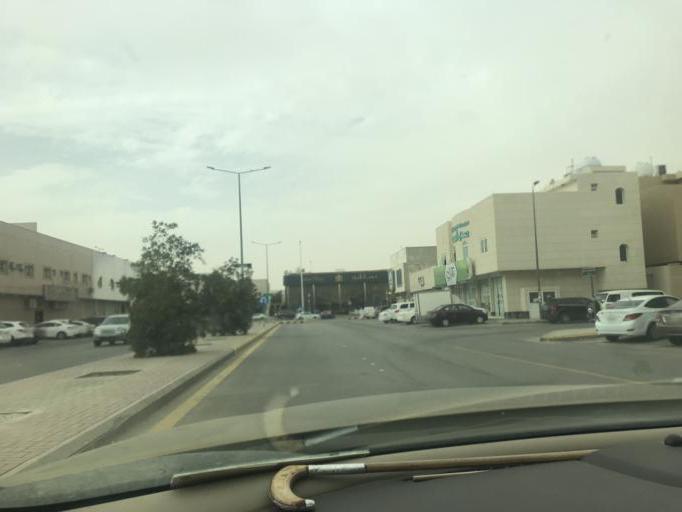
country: SA
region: Ar Riyad
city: Riyadh
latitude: 24.7408
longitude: 46.7523
